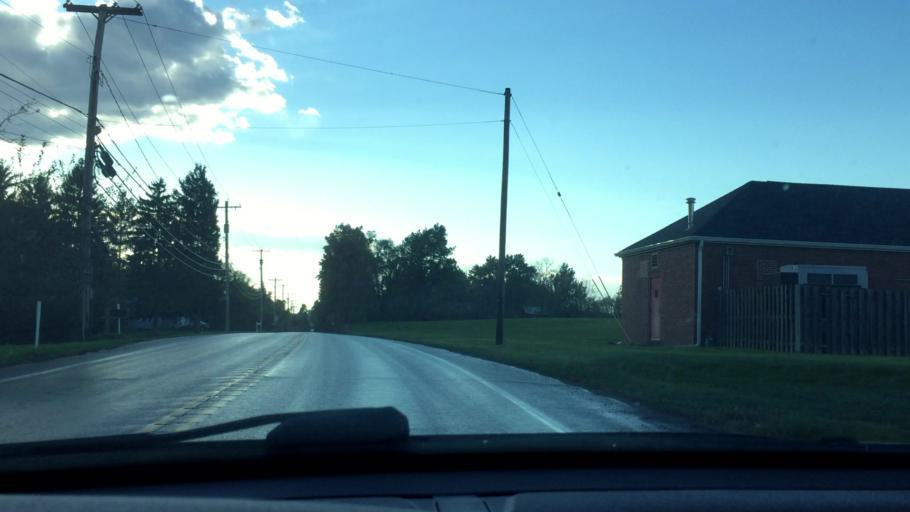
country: US
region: Pennsylvania
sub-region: Lawrence County
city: Bessemer
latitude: 40.9765
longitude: -80.4520
